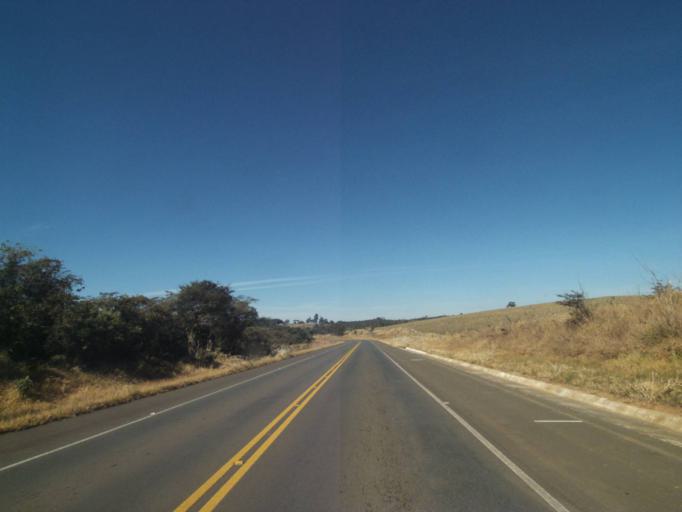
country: BR
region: Parana
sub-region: Tibagi
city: Tibagi
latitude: -24.7687
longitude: -50.4675
